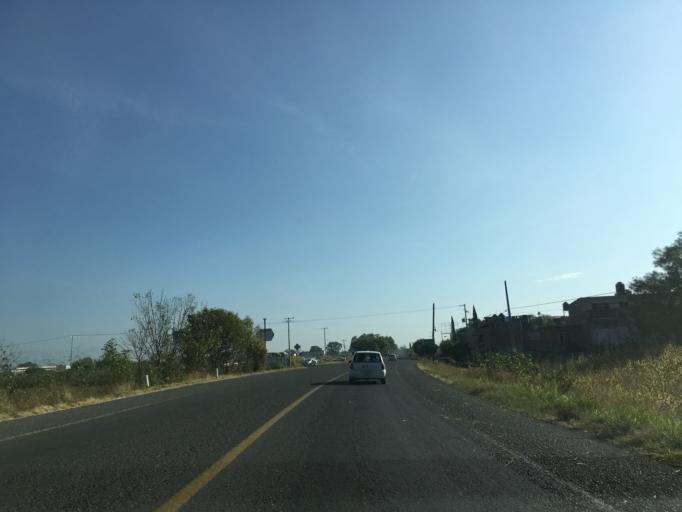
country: MX
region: Michoacan
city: Alvaro Obregon
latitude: 19.8272
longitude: -101.0431
